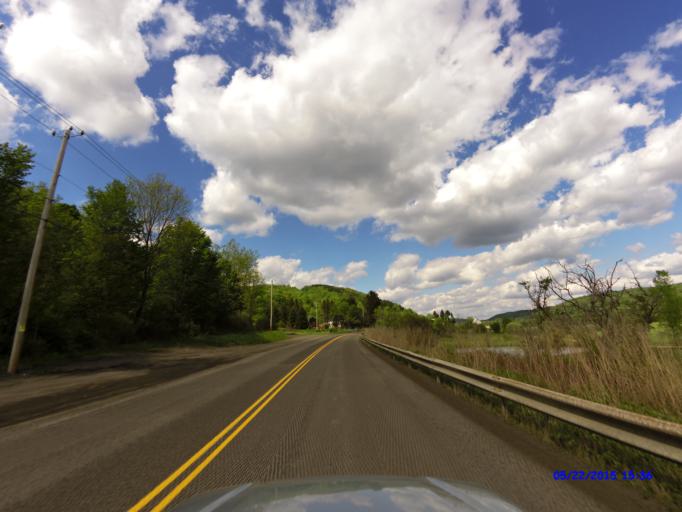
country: US
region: New York
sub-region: Cattaraugus County
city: Salamanca
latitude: 42.2937
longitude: -78.6426
